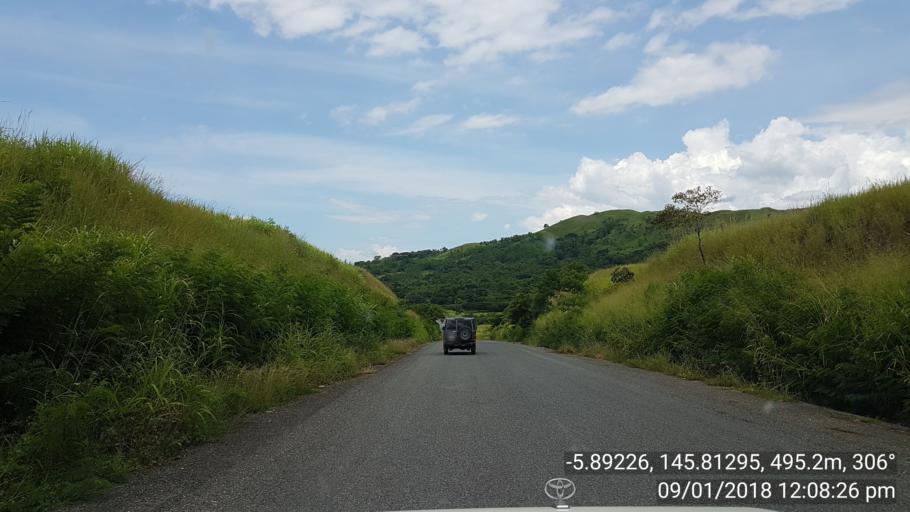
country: PG
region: Eastern Highlands
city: Kainantu
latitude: -5.8922
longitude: 145.8131
